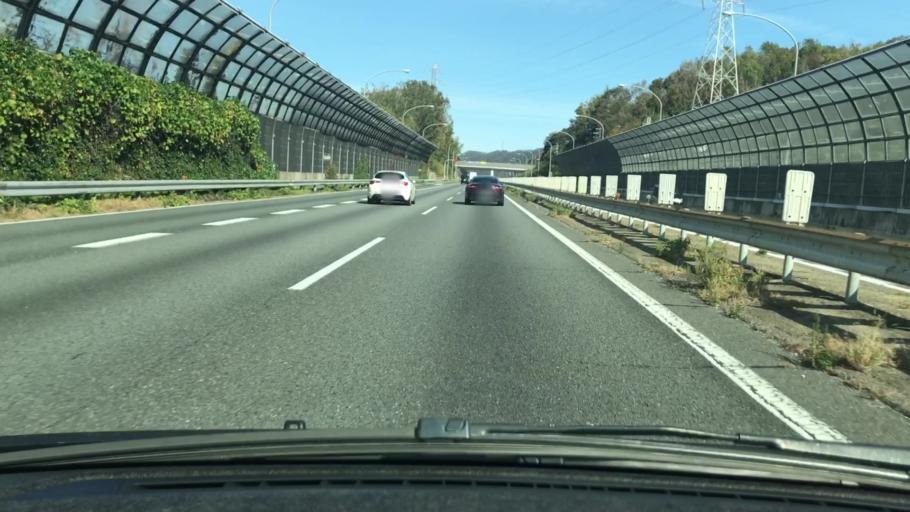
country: JP
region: Shiga Prefecture
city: Otsu-shi
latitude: 34.9740
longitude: 135.8270
